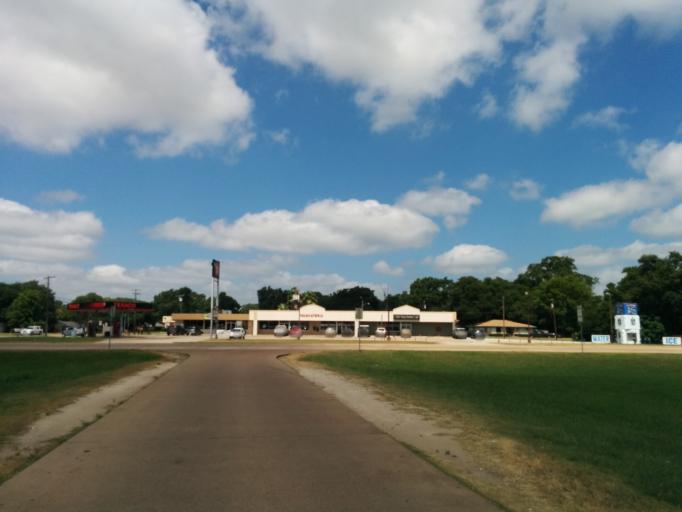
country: US
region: Texas
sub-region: Houston County
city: Crockett
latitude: 31.3157
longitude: -95.4361
